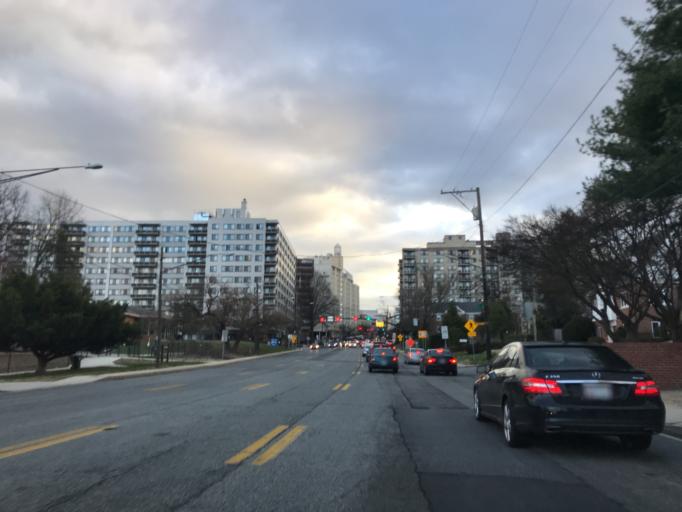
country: US
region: Maryland
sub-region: Montgomery County
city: Silver Spring
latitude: 39.0013
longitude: -77.0253
